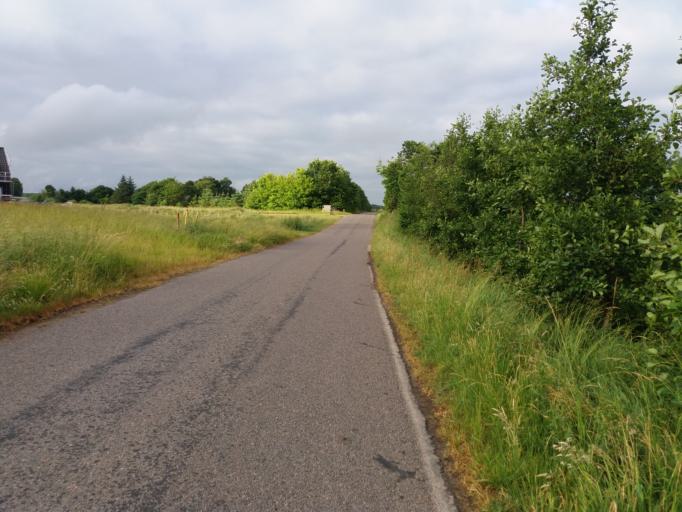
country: DK
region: Central Jutland
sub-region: Skanderborg Kommune
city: Skanderborg
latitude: 56.0764
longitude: 9.8753
